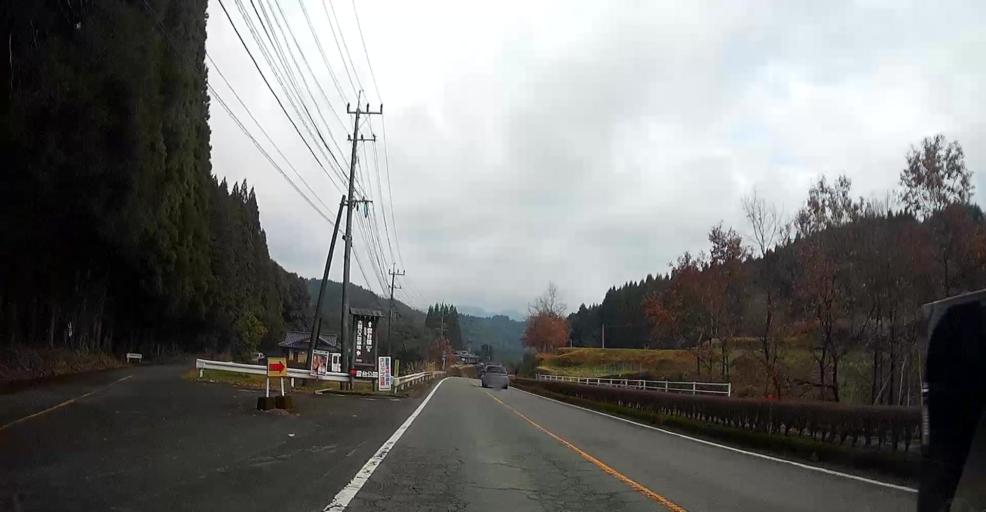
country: JP
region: Kumamoto
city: Matsubase
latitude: 32.6262
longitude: 130.8851
